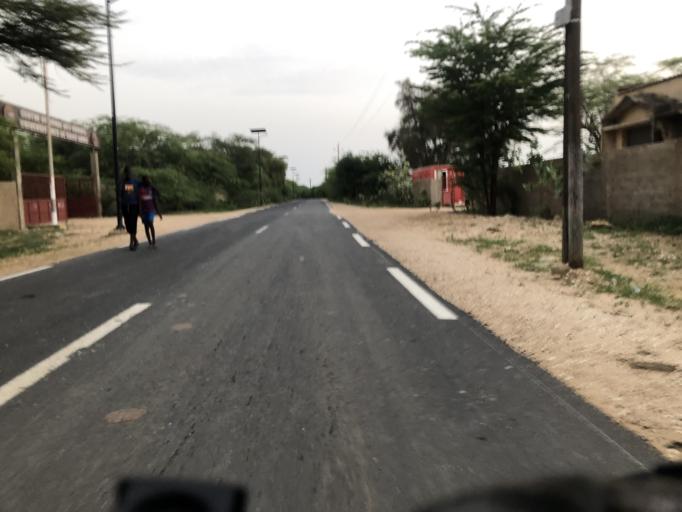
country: SN
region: Saint-Louis
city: Saint-Louis
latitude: 16.0640
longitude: -16.4291
